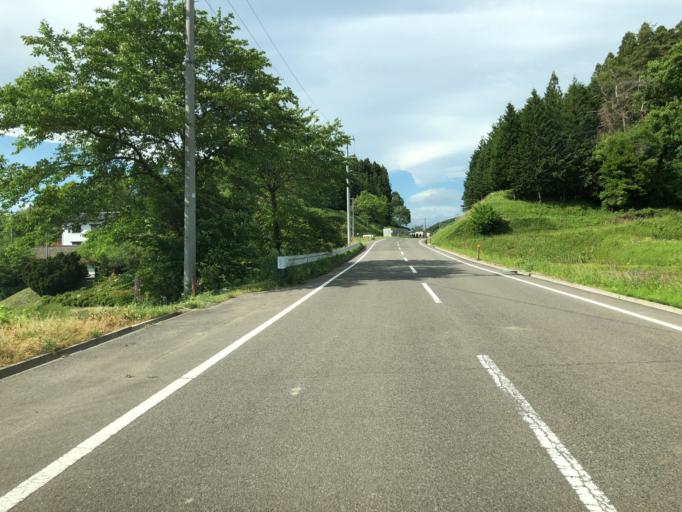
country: JP
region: Fukushima
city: Nihommatsu
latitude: 37.5980
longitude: 140.5176
